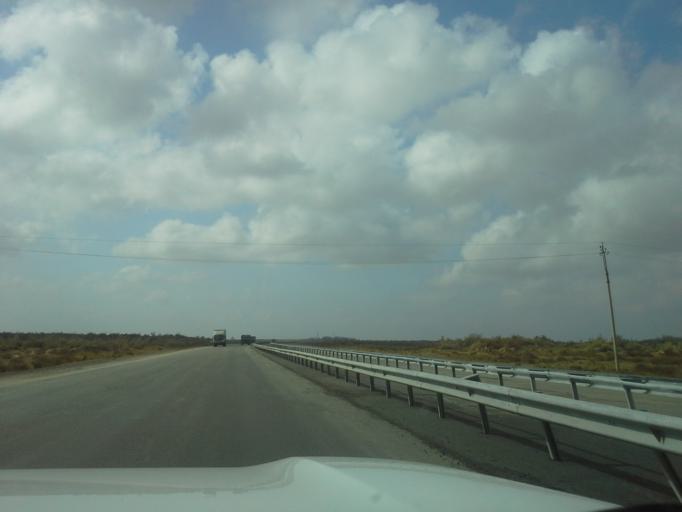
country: TM
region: Mary
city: Mary
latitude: 37.3229
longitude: 61.4098
